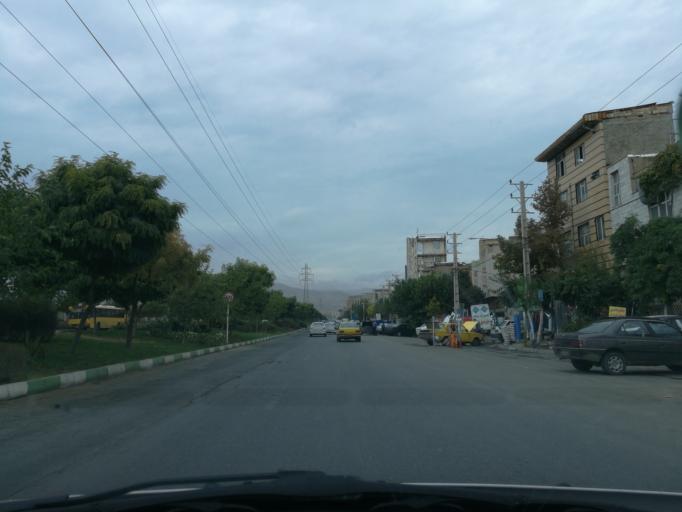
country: IR
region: Alborz
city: Karaj
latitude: 35.8498
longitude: 50.9172
